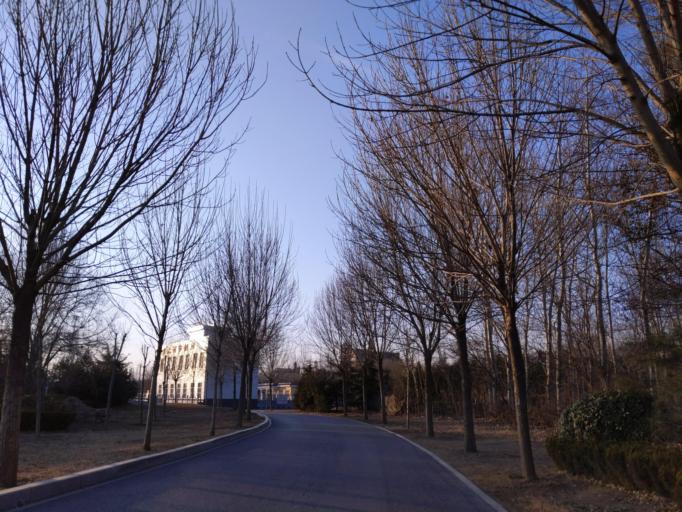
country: CN
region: Henan Sheng
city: Puyang
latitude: 35.7706
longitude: 114.9961
